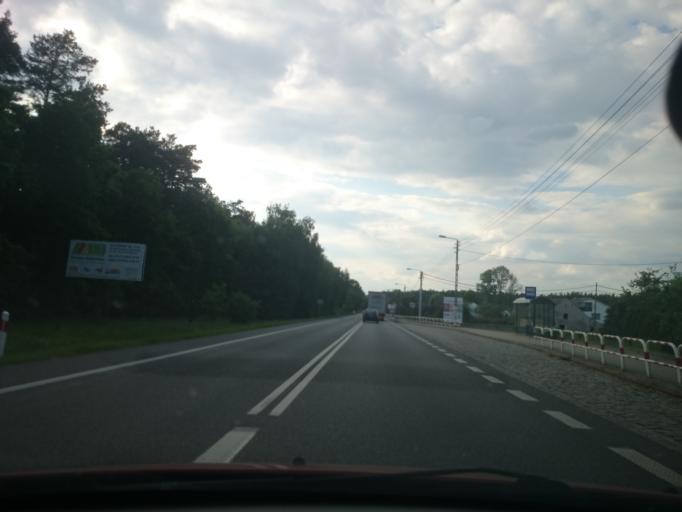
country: PL
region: Opole Voivodeship
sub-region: Powiat opolski
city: Tarnow Opolski
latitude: 50.6078
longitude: 18.0724
